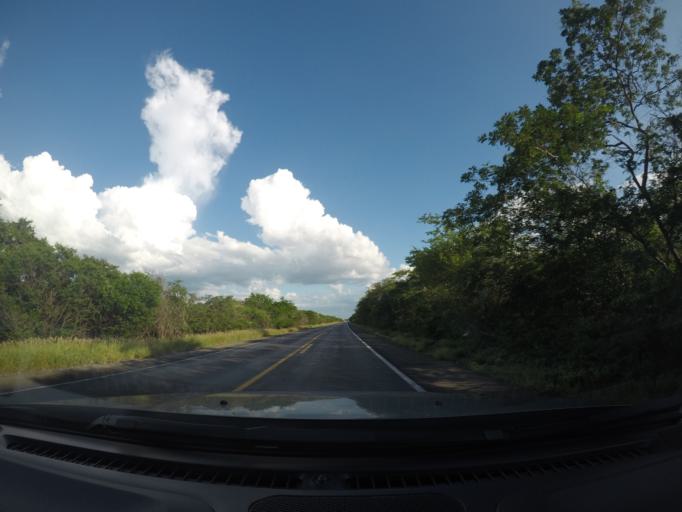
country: BR
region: Bahia
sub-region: Oliveira Dos Brejinhos
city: Oliveira dos Brejinhos
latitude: -12.0926
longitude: -42.9279
